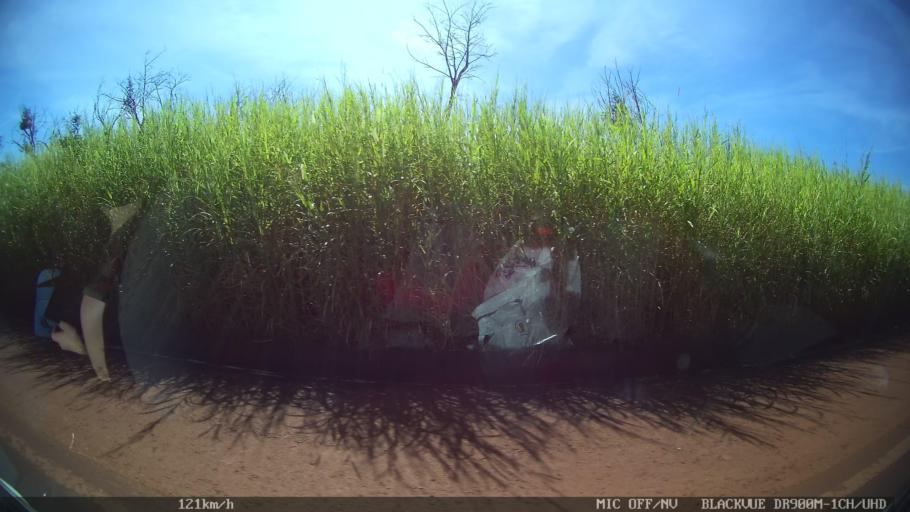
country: BR
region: Sao Paulo
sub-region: Sao Joaquim Da Barra
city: Sao Joaquim da Barra
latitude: -20.5433
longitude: -47.7914
